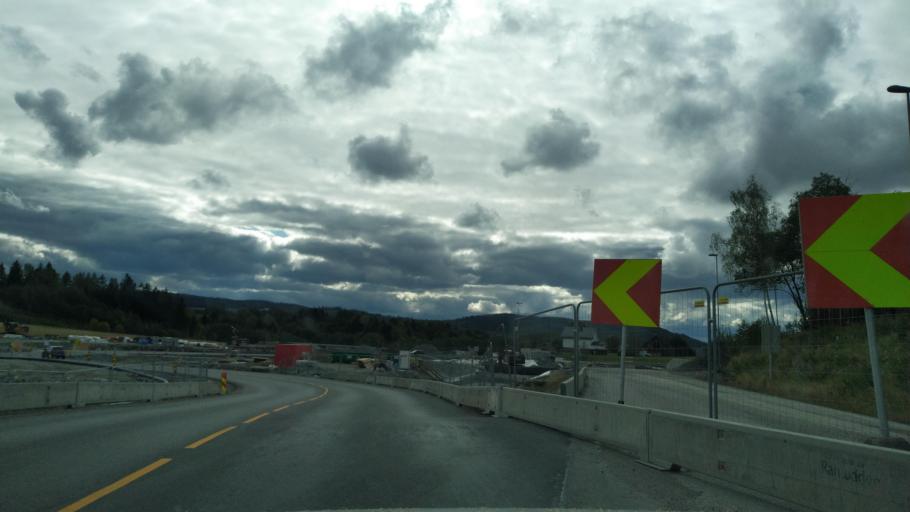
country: NO
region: Akershus
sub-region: Sorum
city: Frogner
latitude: 60.0239
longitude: 11.1164
